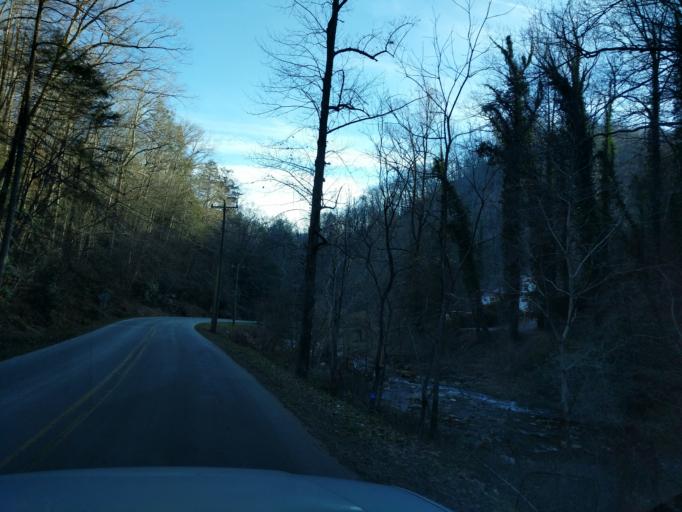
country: US
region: North Carolina
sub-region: Henderson County
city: Edneyville
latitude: 35.4542
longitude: -82.2980
